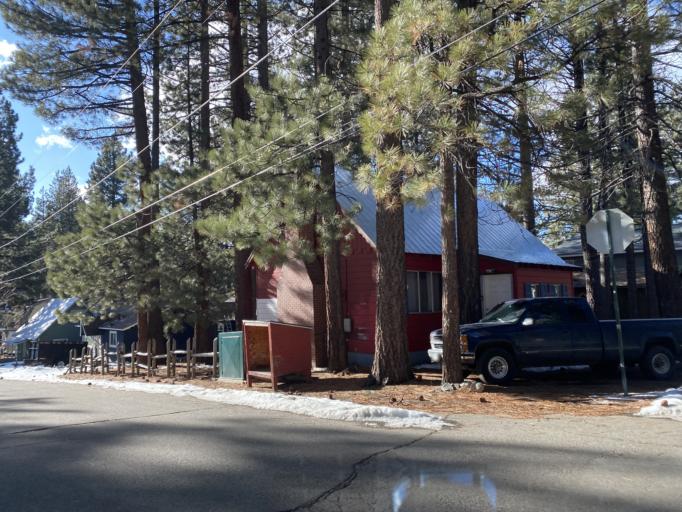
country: US
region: California
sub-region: El Dorado County
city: South Lake Tahoe
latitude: 38.9238
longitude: -119.9820
